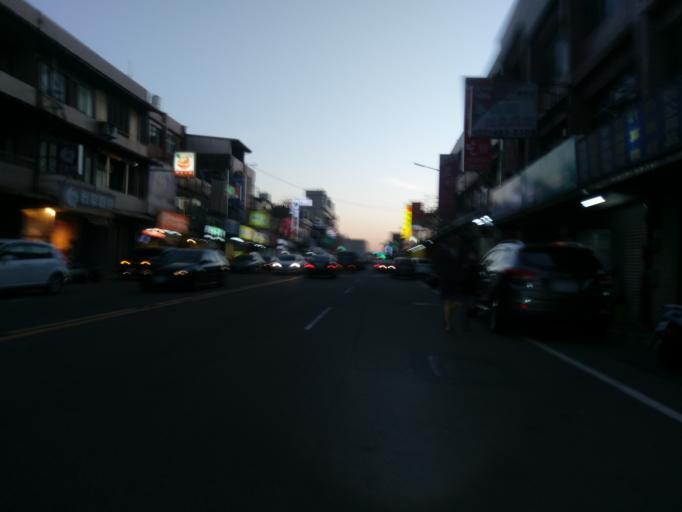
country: TW
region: Taiwan
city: Taoyuan City
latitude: 25.0470
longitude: 121.1422
